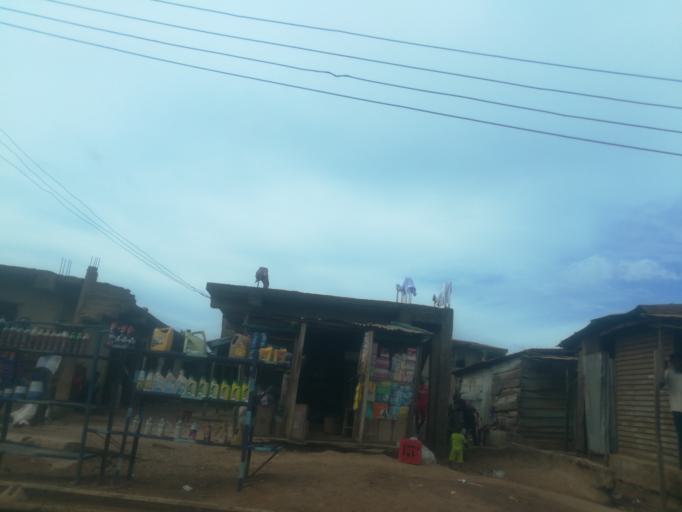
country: NG
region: Oyo
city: Ibadan
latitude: 7.3780
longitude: 3.9428
